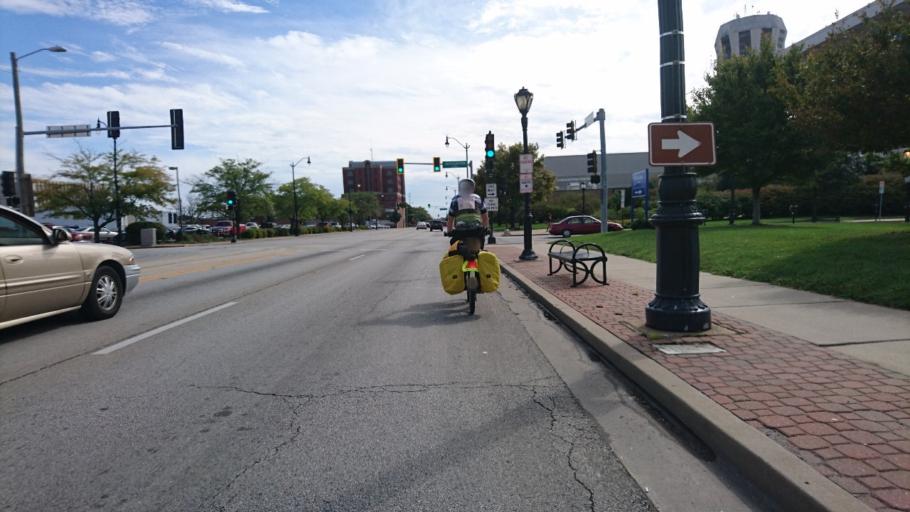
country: US
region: Illinois
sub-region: Sangamon County
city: Springfield
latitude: 39.8032
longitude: -89.6437
